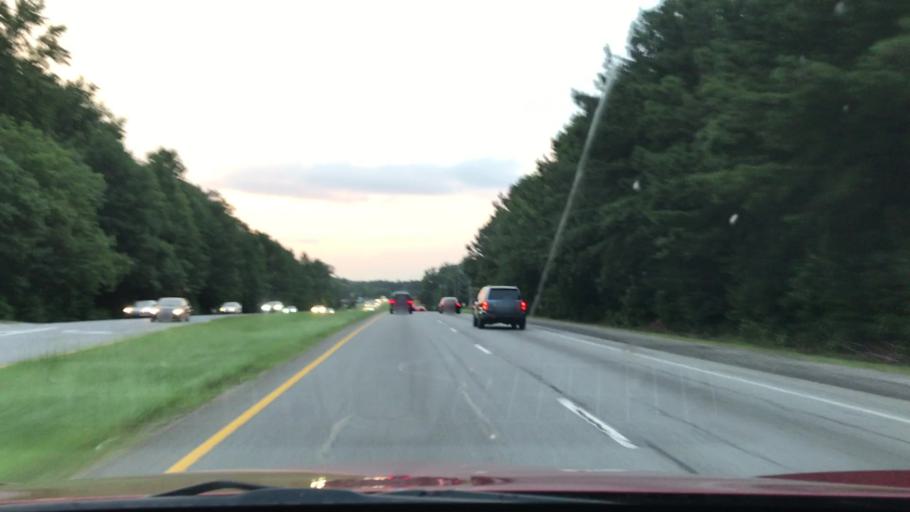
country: US
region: Georgia
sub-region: Gwinnett County
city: Sugar Hill
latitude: 34.0460
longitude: -83.9925
